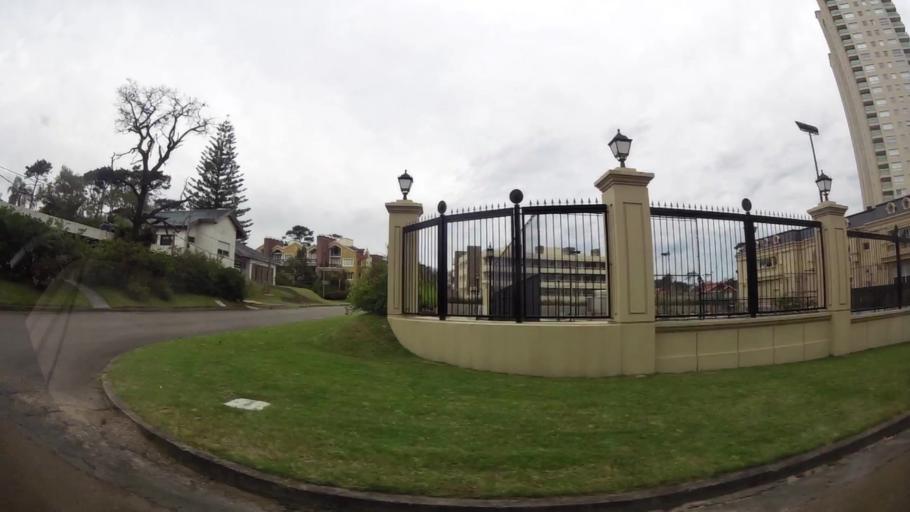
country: UY
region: Maldonado
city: Maldonado
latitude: -34.9301
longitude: -54.9558
